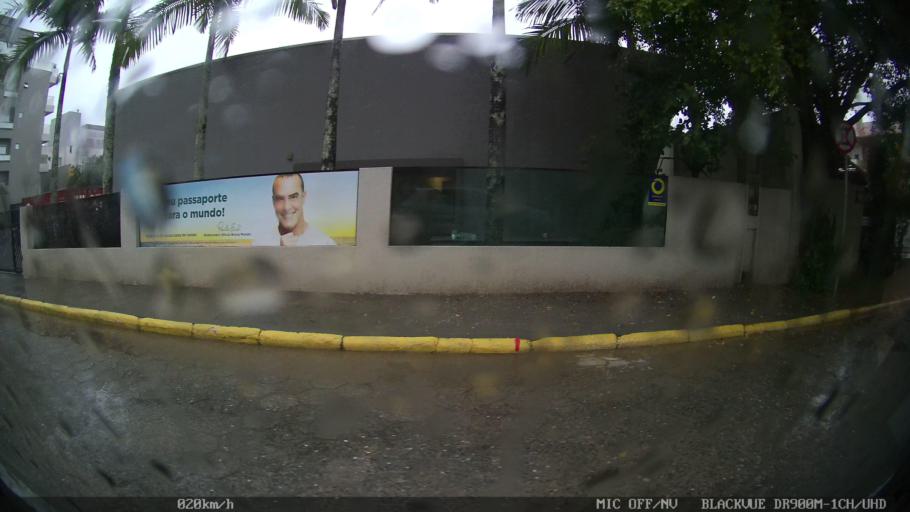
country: BR
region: Santa Catarina
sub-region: Balneario Camboriu
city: Balneario Camboriu
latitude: -26.9502
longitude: -48.6307
